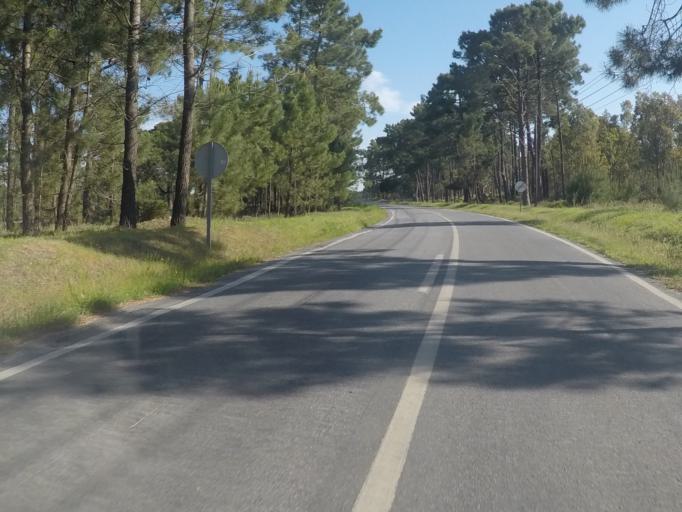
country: PT
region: Setubal
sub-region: Sesimbra
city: Sesimbra
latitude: 38.4882
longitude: -9.1577
